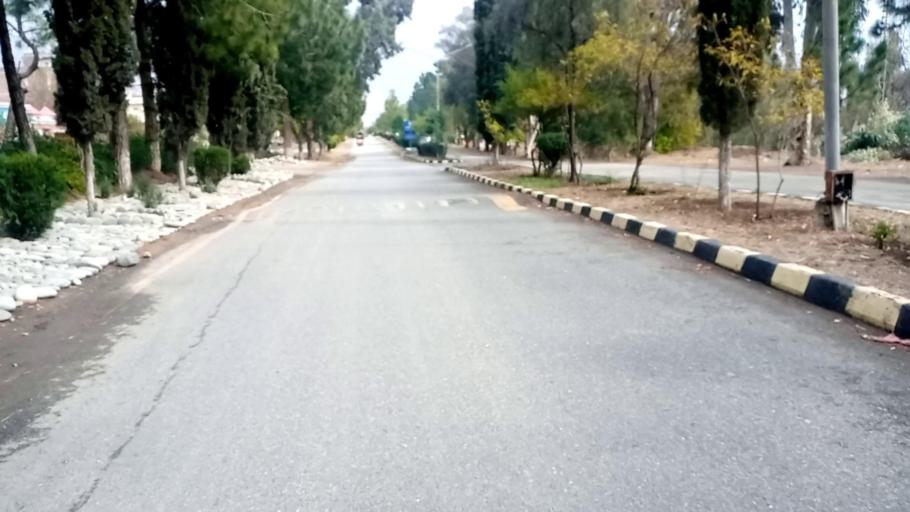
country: PK
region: Khyber Pakhtunkhwa
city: Mingora
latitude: 34.8309
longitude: 72.3492
